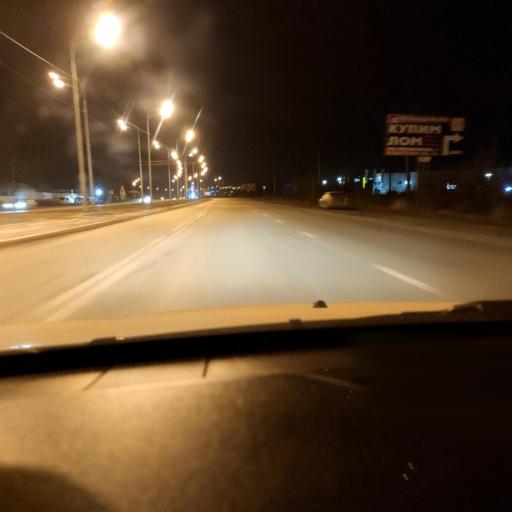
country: RU
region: Samara
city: Smyshlyayevka
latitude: 53.2601
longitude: 50.3776
